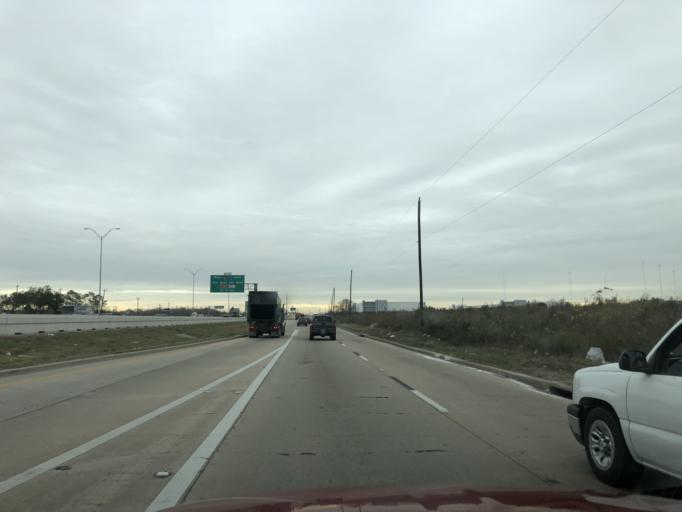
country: US
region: Texas
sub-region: Fort Bend County
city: Missouri City
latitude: 29.6336
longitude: -95.5269
